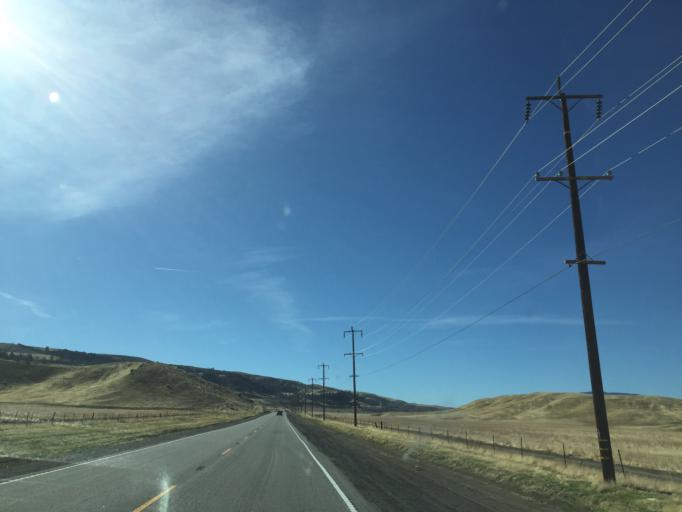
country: US
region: California
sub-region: Kern County
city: Lebec
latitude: 34.7702
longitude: -118.7003
